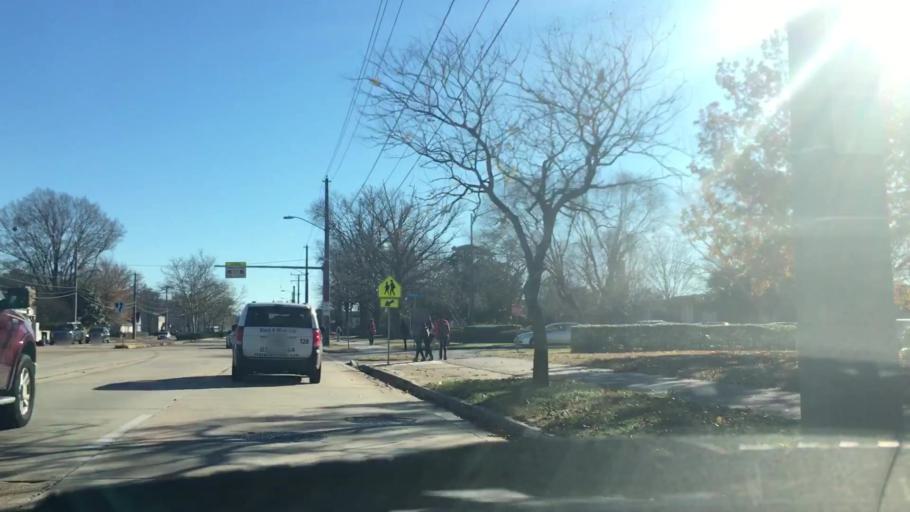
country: US
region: Virginia
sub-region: City of Norfolk
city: Norfolk
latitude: 36.8985
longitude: -76.2390
